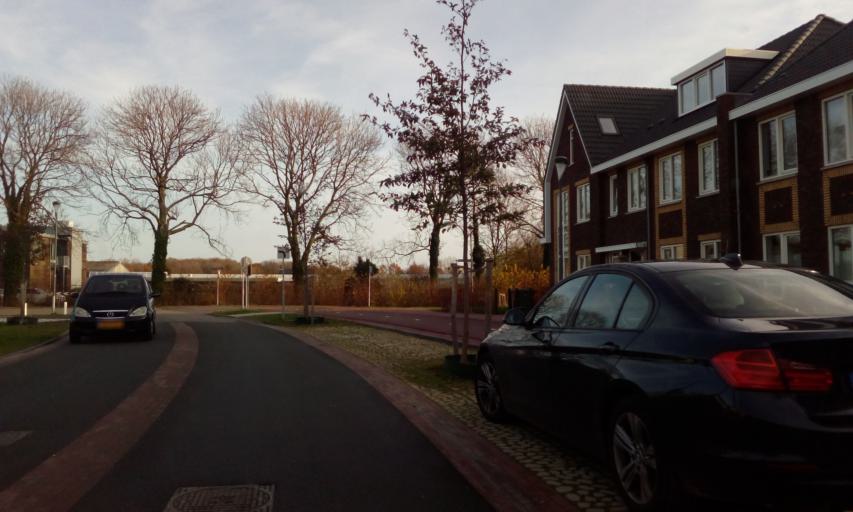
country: NL
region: South Holland
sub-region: Gemeente Rijswijk
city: Rijswijk
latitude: 52.0202
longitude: 4.3238
